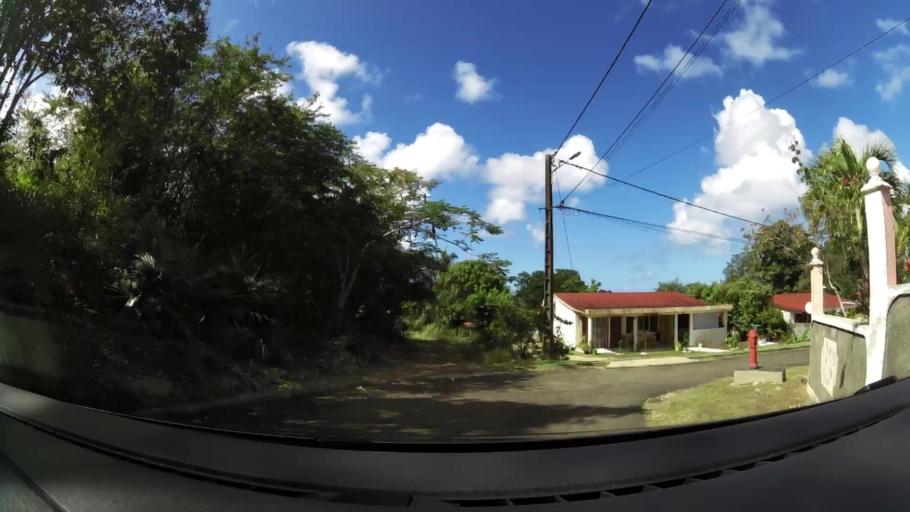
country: GP
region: Guadeloupe
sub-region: Guadeloupe
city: Anse-Bertrand
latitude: 16.4681
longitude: -61.5141
